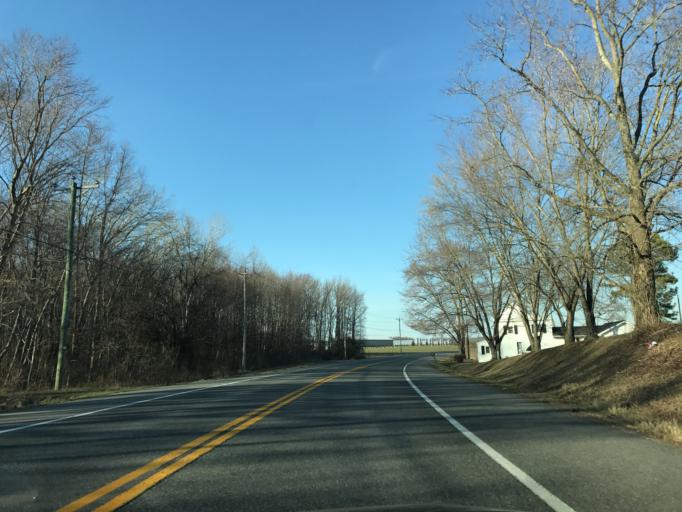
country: US
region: Maryland
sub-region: Caroline County
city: Greensboro
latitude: 39.1525
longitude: -75.8666
